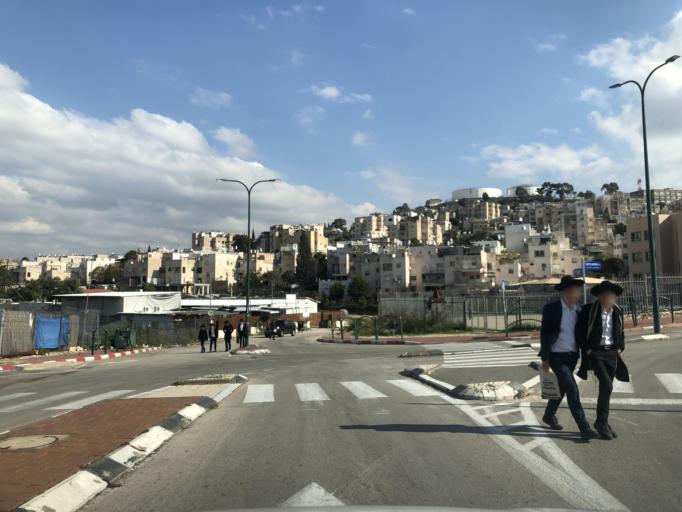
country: IL
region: Jerusalem
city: Modiin Ilit
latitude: 31.9345
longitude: 35.0382
